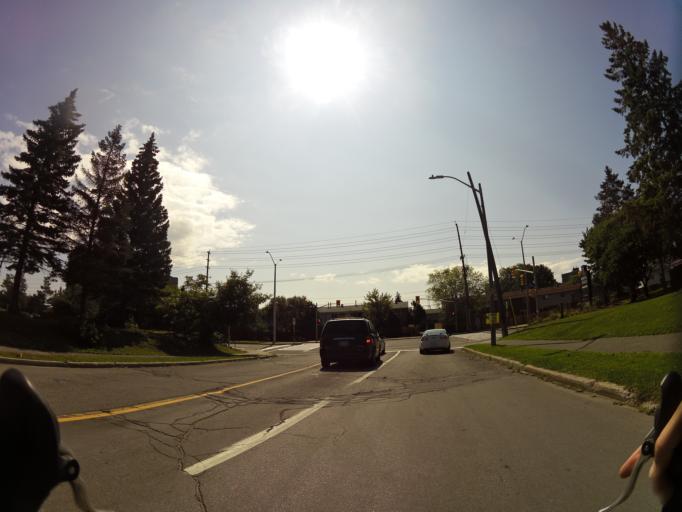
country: CA
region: Ontario
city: Ottawa
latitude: 45.3753
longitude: -75.6525
